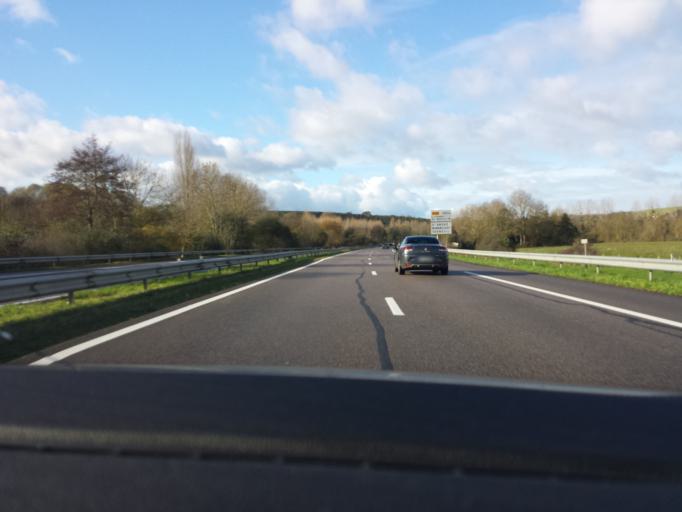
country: FR
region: Haute-Normandie
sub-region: Departement de l'Eure
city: Pacy-sur-Eure
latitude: 49.0077
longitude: 1.3743
